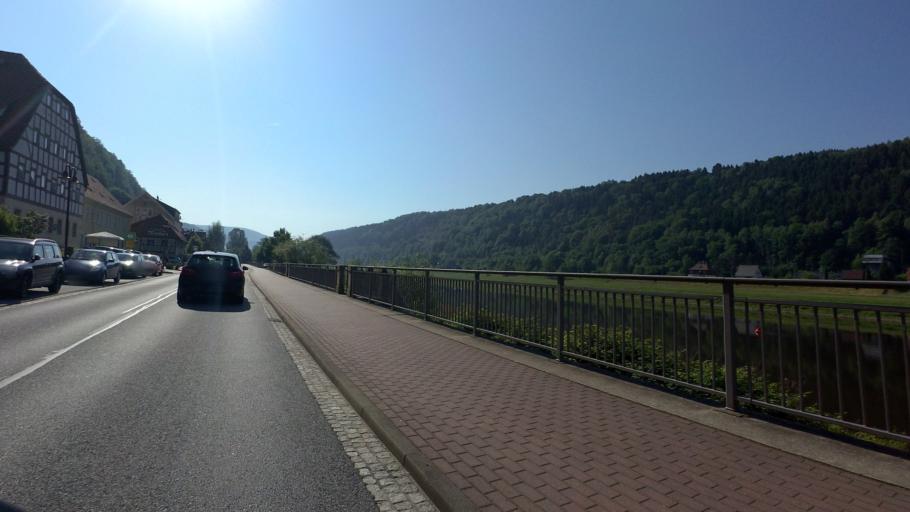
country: DE
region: Saxony
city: Bad Schandau
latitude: 50.9125
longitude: 14.1759
